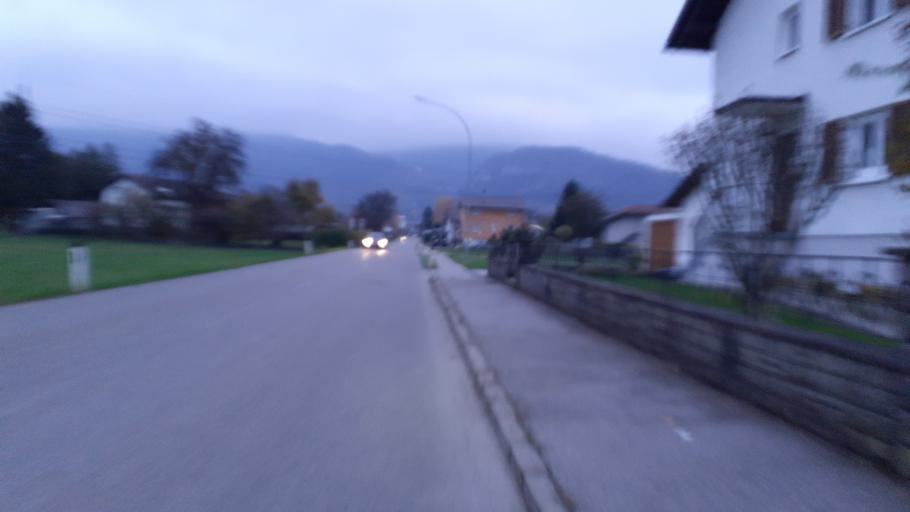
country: AT
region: Vorarlberg
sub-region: Politischer Bezirk Feldkirch
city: Mader
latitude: 47.3428
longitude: 9.6257
